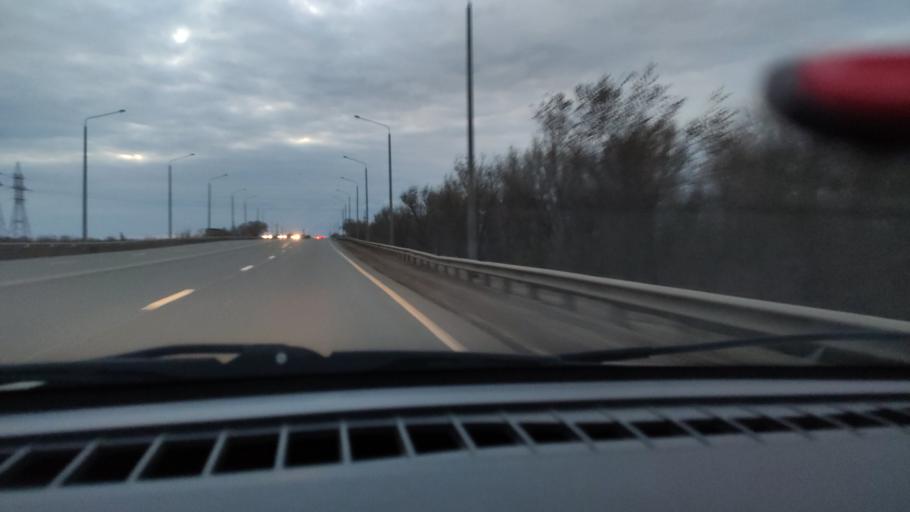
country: RU
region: Orenburg
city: Orenburg
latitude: 51.8510
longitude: 55.1422
